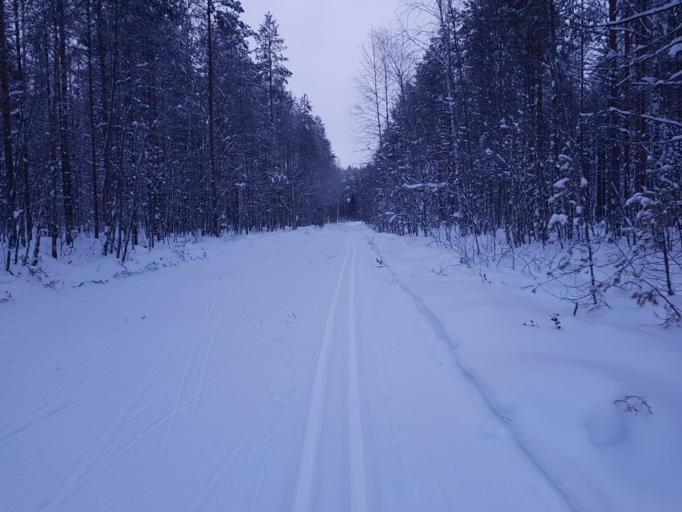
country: FI
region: Kainuu
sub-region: Kehys-Kainuu
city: Kuhmo
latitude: 64.1148
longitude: 29.5685
